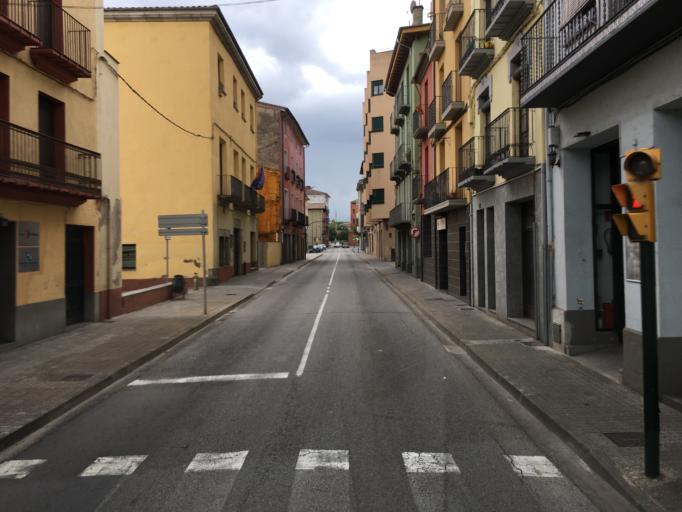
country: ES
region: Catalonia
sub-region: Provincia de Girona
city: Olot
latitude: 42.1830
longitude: 2.4934
